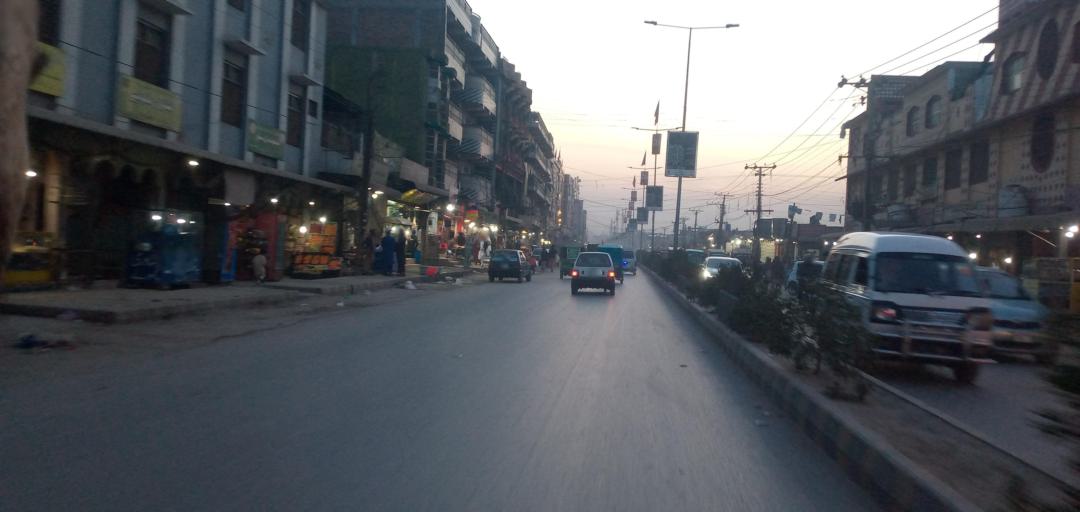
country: PK
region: Khyber Pakhtunkhwa
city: Peshawar
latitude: 34.0294
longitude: 71.6021
